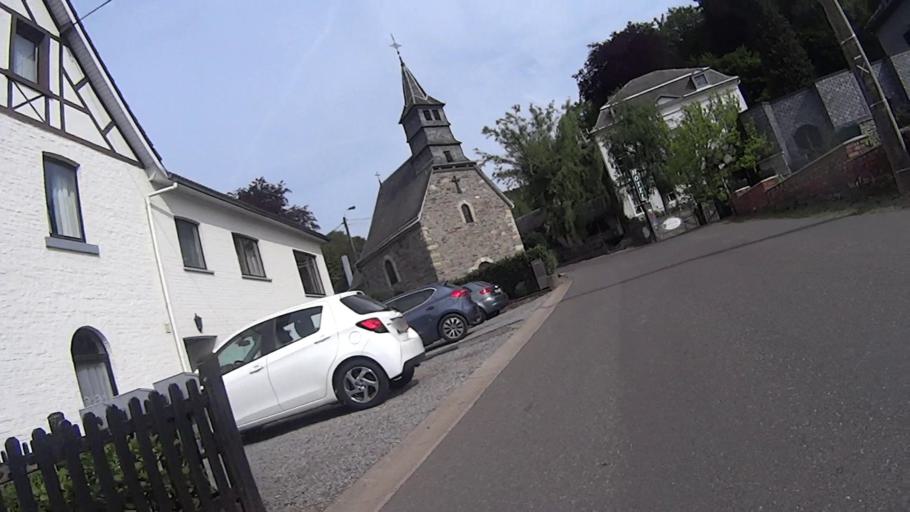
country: BE
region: Wallonia
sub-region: Province de Liege
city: Malmedy
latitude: 50.4415
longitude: 6.0389
